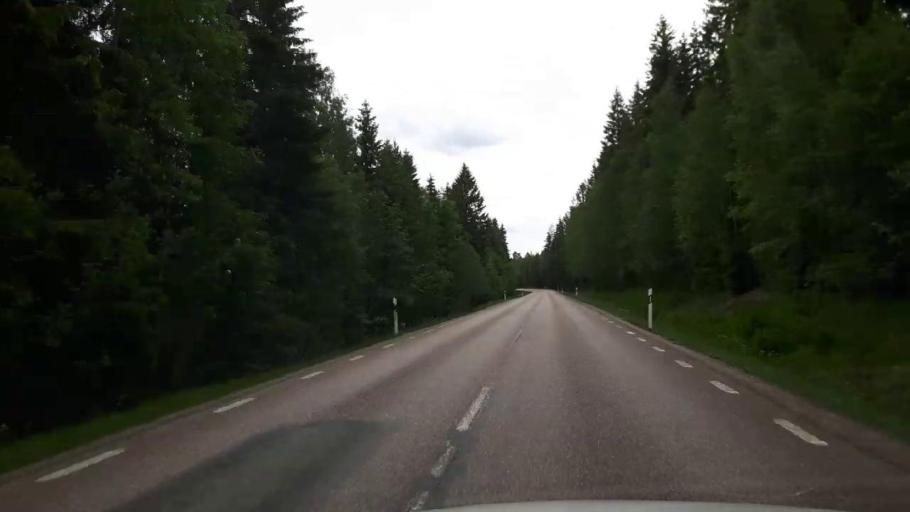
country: SE
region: Dalarna
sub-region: Hedemora Kommun
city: Brunna
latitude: 60.1828
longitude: 15.9992
